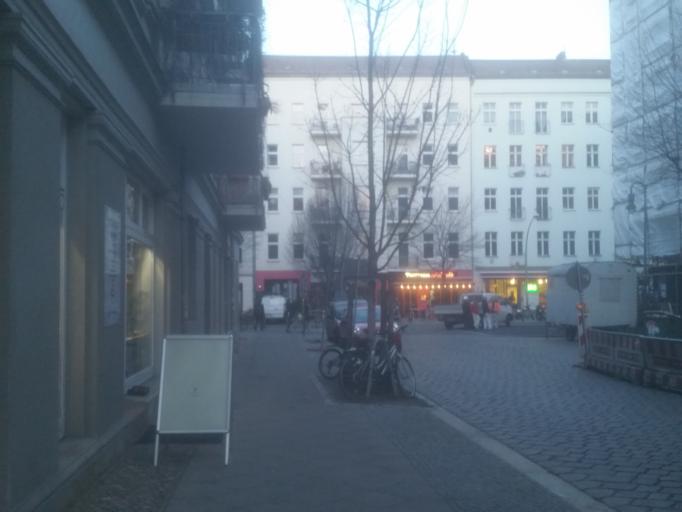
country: DE
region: Berlin
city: Prenzlauer Berg Bezirk
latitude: 52.5448
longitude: 13.4210
